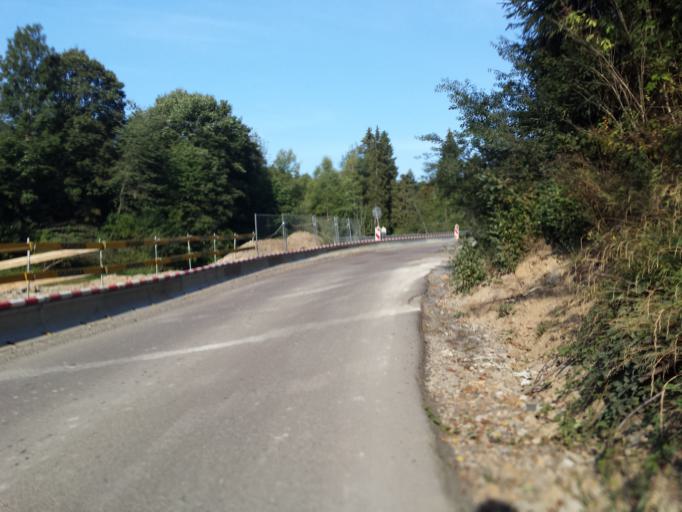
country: PL
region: Subcarpathian Voivodeship
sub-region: Powiat leski
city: Cisna
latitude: 49.2158
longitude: 22.3250
